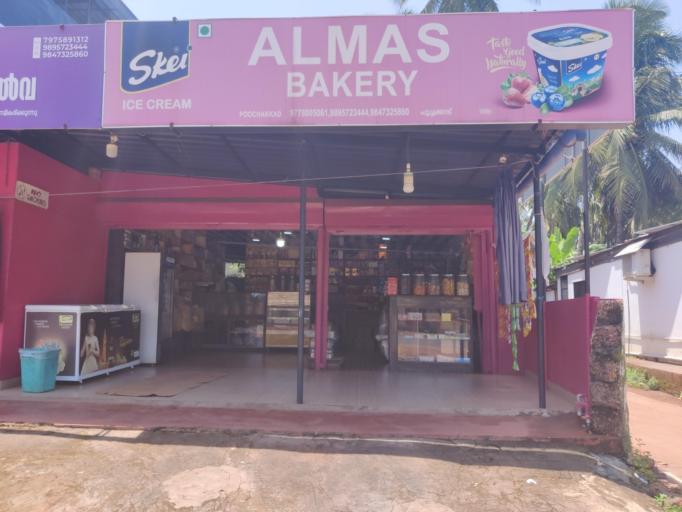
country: IN
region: Kerala
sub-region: Kasaragod District
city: Kannangad
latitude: 12.3802
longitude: 75.0508
